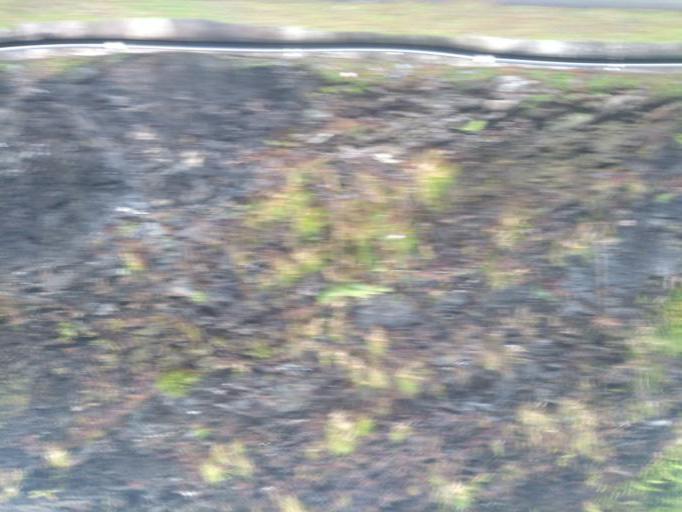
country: MY
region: Pahang
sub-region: Cameron Highlands
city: Tanah Rata
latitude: 4.6007
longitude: 101.3414
